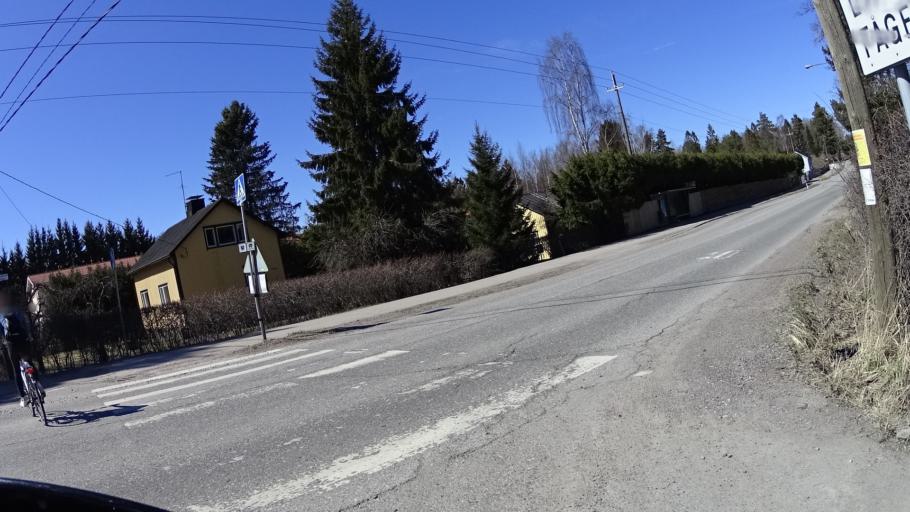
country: FI
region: Uusimaa
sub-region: Helsinki
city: Kilo
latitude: 60.2409
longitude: 24.8088
